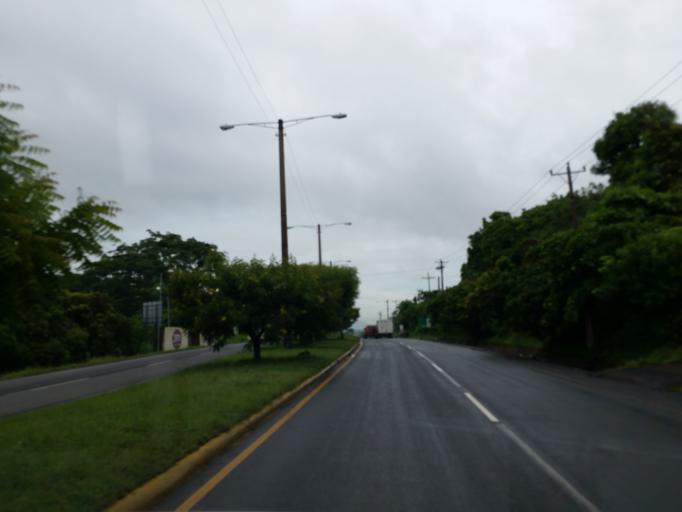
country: NI
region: Managua
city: Ciudad Sandino
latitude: 12.1723
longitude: -86.3454
